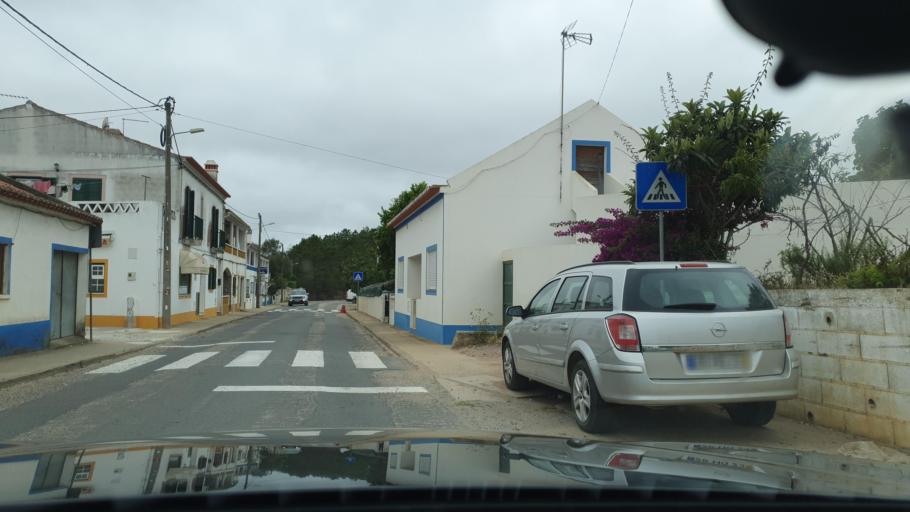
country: PT
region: Beja
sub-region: Odemira
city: Sao Teotonio
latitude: 37.5062
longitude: -8.6943
